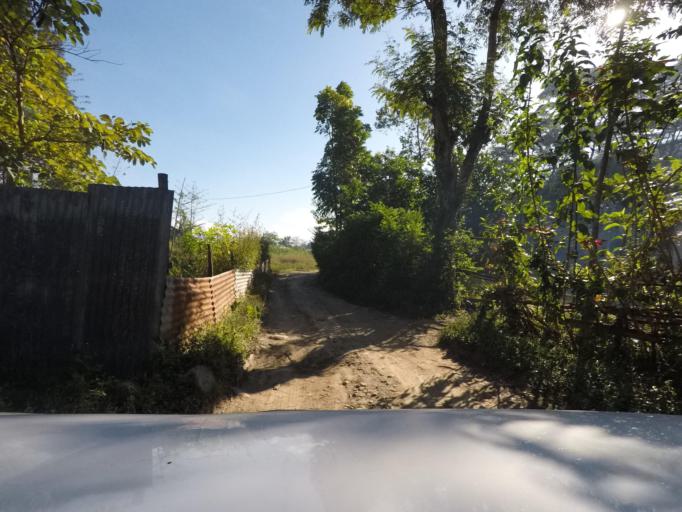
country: TL
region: Ermera
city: Gleno
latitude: -8.7337
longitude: 125.4313
